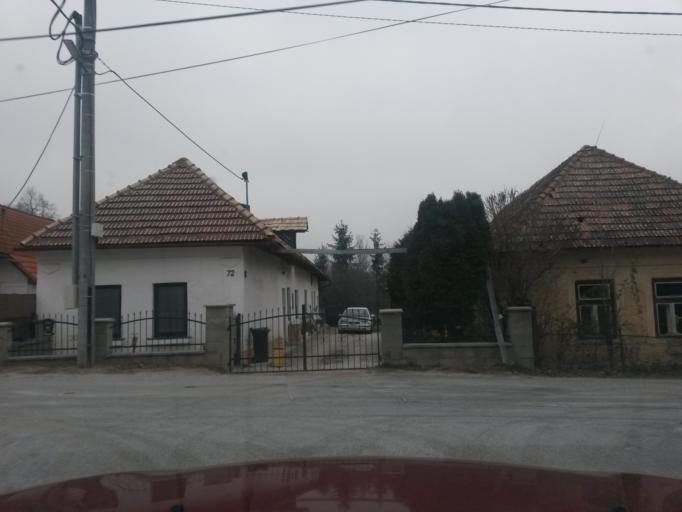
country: SK
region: Kosicky
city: Roznava
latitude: 48.6794
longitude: 20.5164
